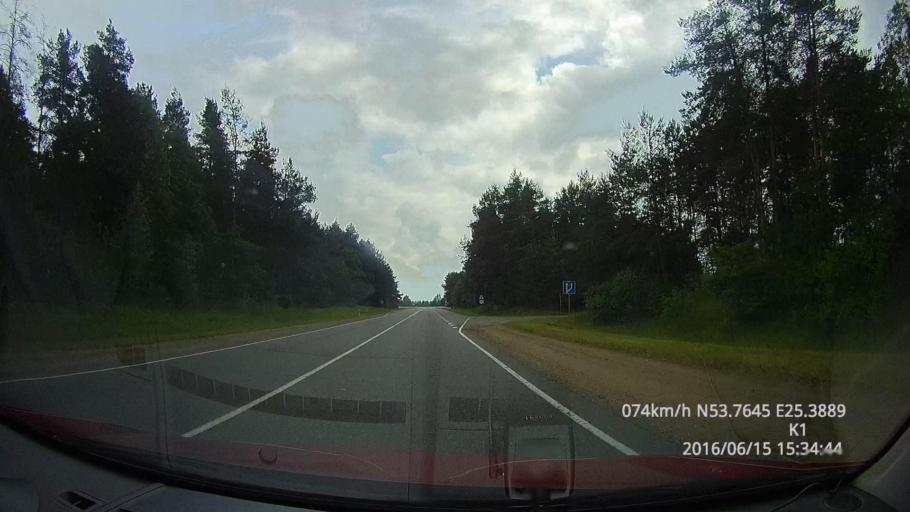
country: BY
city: Berezovka
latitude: 53.7638
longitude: 25.3892
